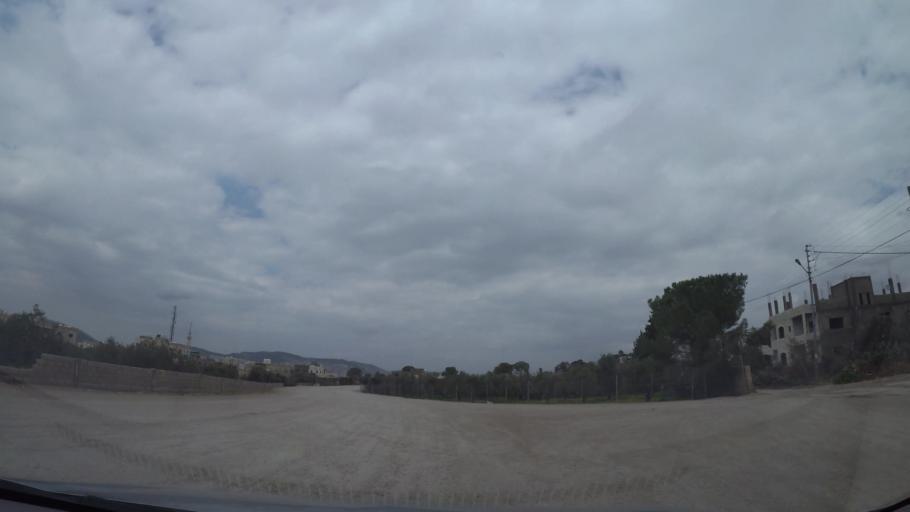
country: JO
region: Amman
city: Al Jubayhah
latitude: 32.0555
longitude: 35.8400
